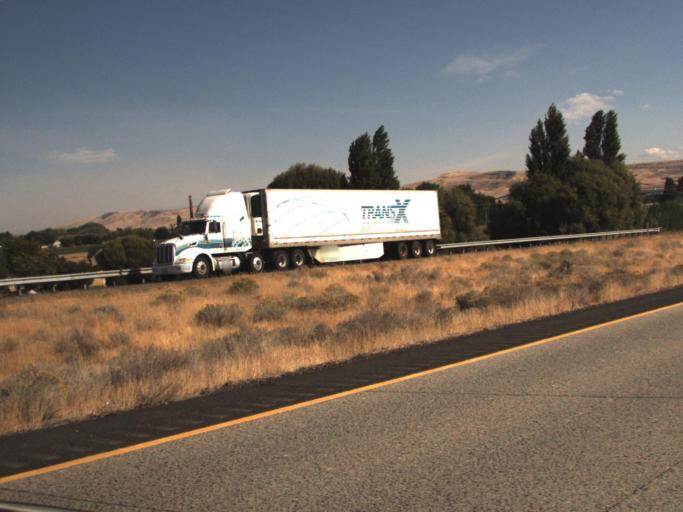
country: US
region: Washington
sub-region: Benton County
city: Prosser
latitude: 46.2351
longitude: -119.8135
